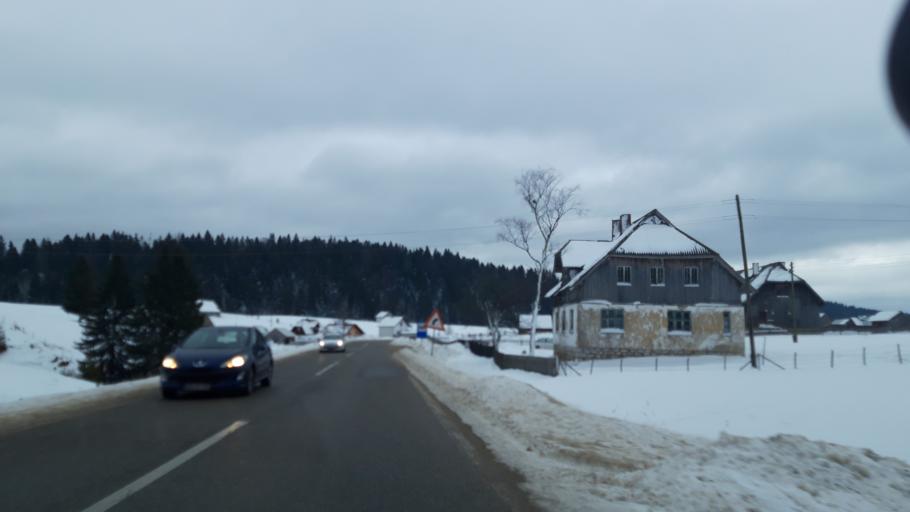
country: BA
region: Republika Srpska
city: Han Pijesak
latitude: 44.1086
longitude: 18.9694
